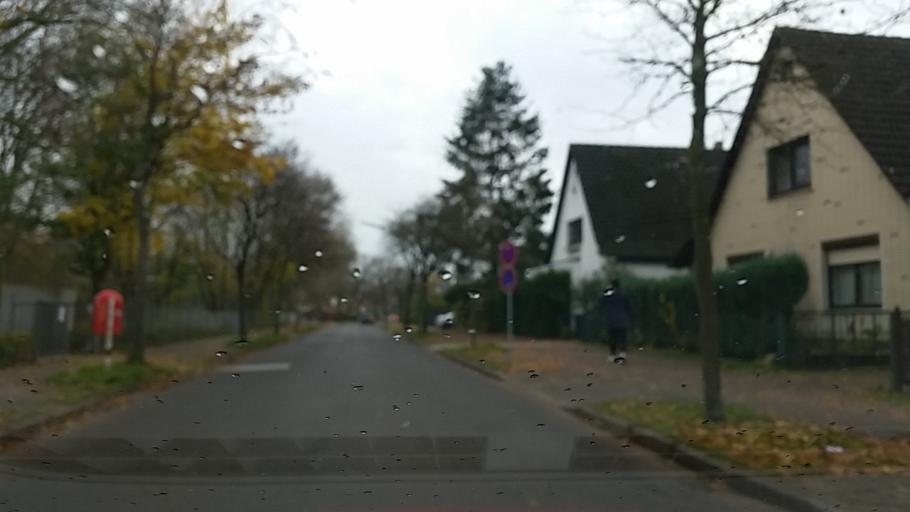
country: DE
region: Hamburg
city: Wandsbek
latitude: 53.5561
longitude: 10.1023
